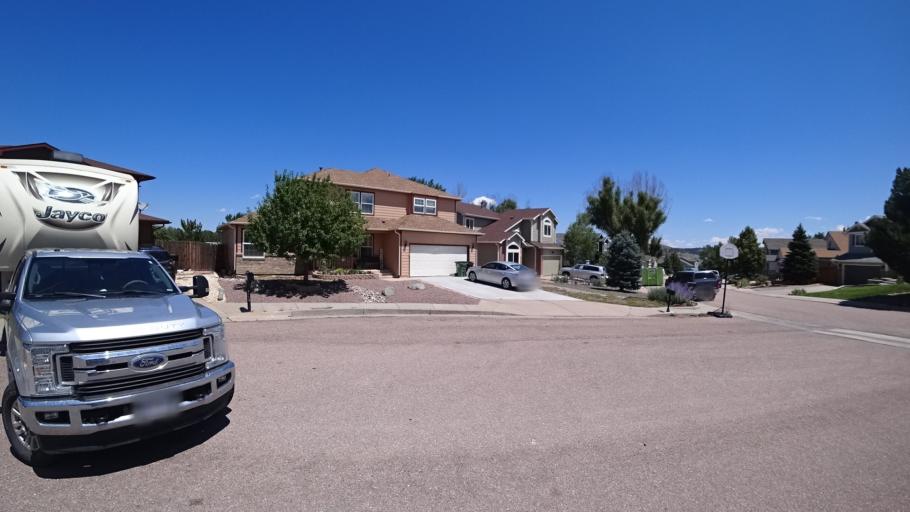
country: US
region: Colorado
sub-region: El Paso County
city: Air Force Academy
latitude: 38.9202
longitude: -104.8361
